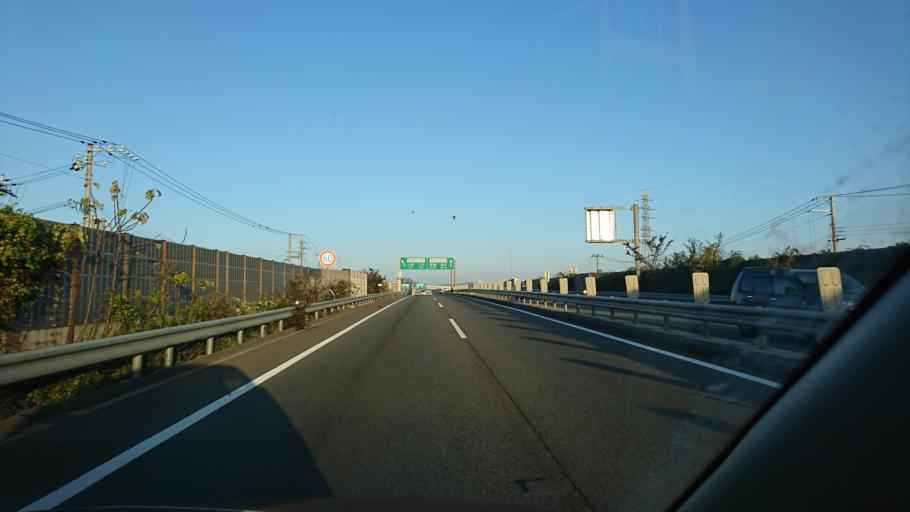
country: JP
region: Hyogo
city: Kakogawacho-honmachi
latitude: 34.7582
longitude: 134.8587
